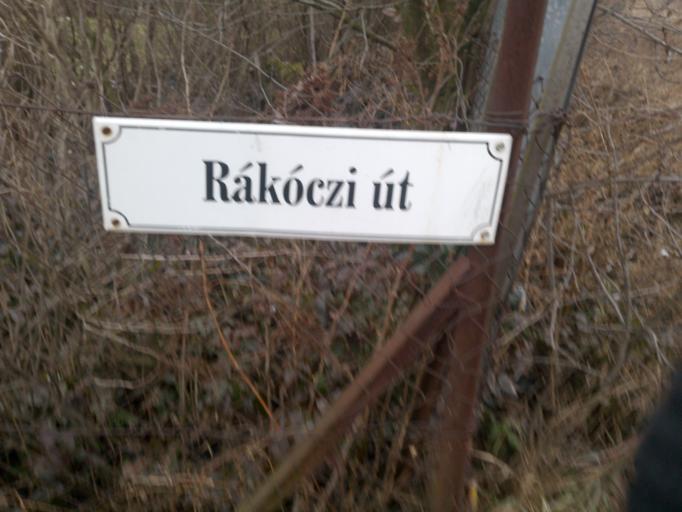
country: HU
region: Borsod-Abauj-Zemplen
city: Encs
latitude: 48.3297
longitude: 21.1312
